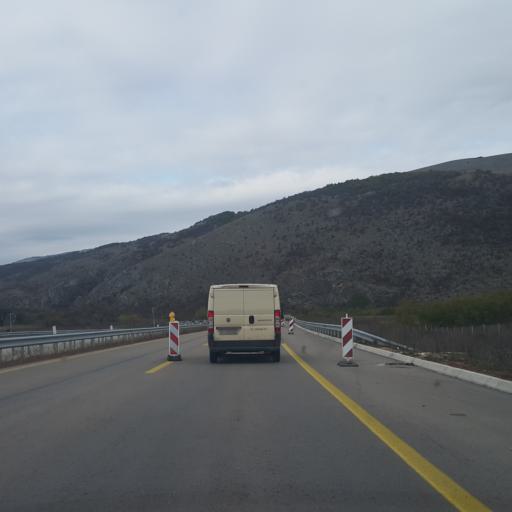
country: RS
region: Central Serbia
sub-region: Pirotski Okrug
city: Bela Palanka
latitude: 43.2296
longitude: 22.3809
